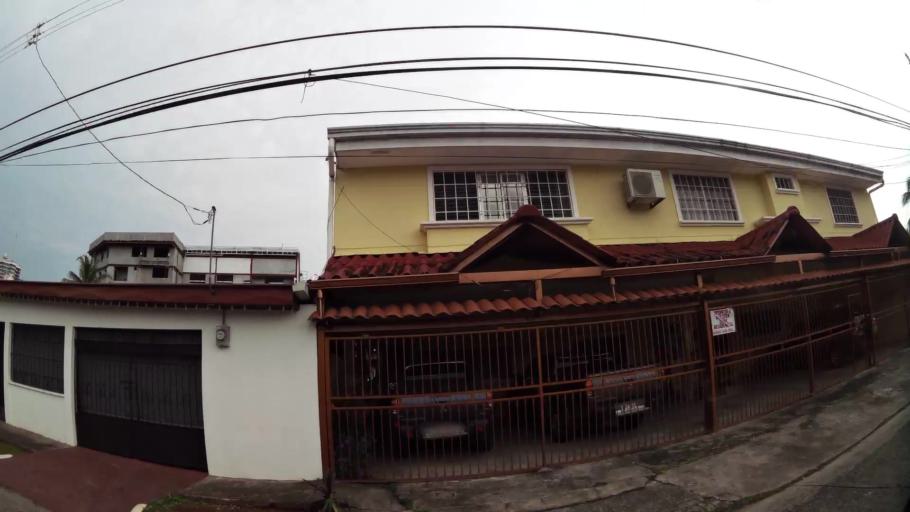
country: PA
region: Panama
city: Panama
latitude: 9.0135
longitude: -79.5231
